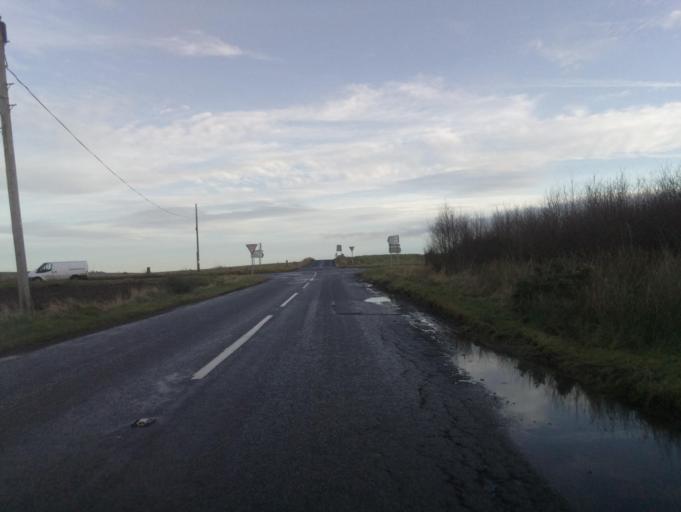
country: GB
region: Scotland
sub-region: Angus
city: Letham
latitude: 56.5775
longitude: -2.7807
